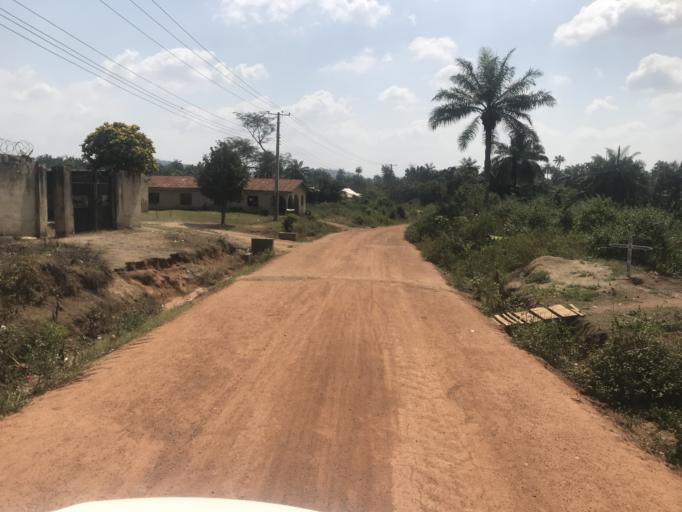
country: NG
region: Osun
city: Iragbiji
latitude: 7.8865
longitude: 4.7012
